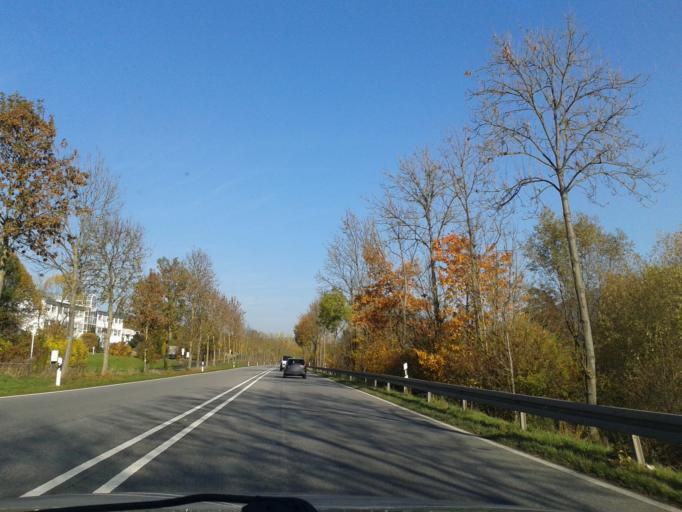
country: DE
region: Hesse
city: Dillenburg
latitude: 50.7782
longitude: 8.3088
